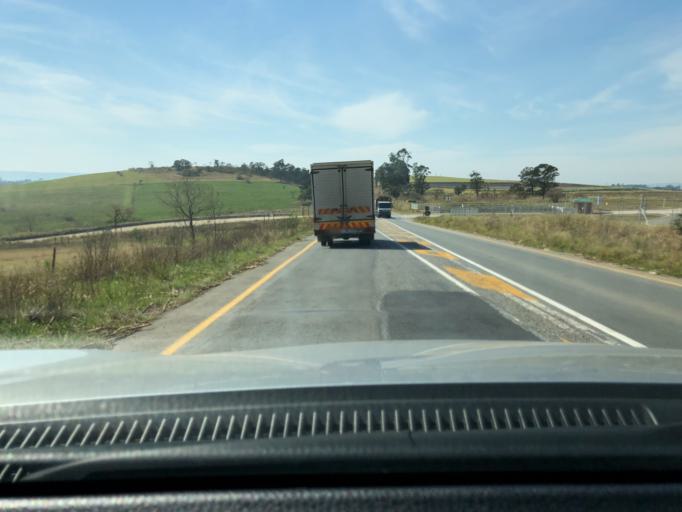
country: ZA
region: KwaZulu-Natal
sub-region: uMgungundlovu District Municipality
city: Camperdown
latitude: -29.7230
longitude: 30.4756
